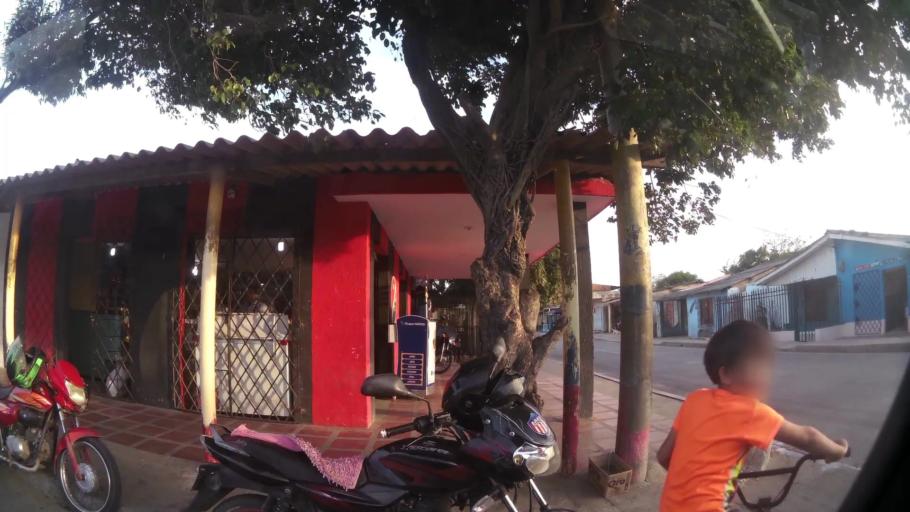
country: CO
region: Atlantico
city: Barranquilla
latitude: 10.9590
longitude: -74.8256
